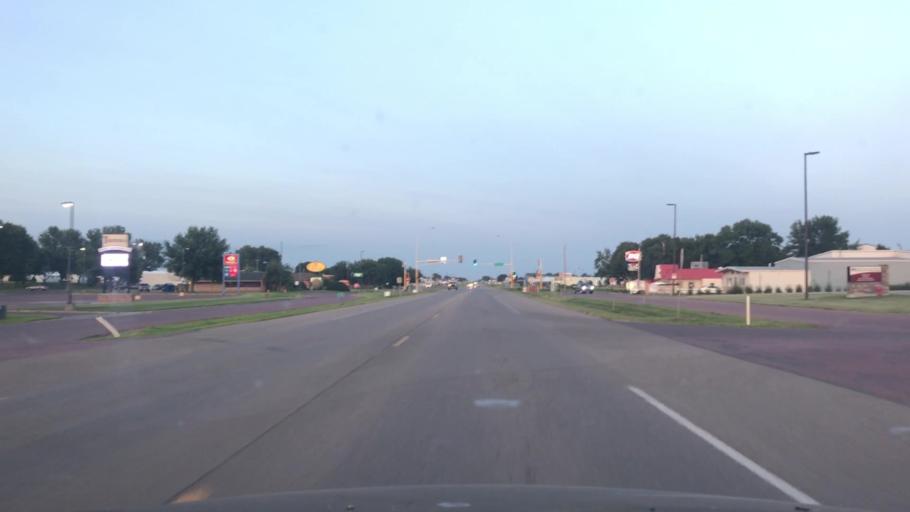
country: US
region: Minnesota
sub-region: Redwood County
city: Redwood Falls
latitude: 44.5414
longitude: -95.1028
